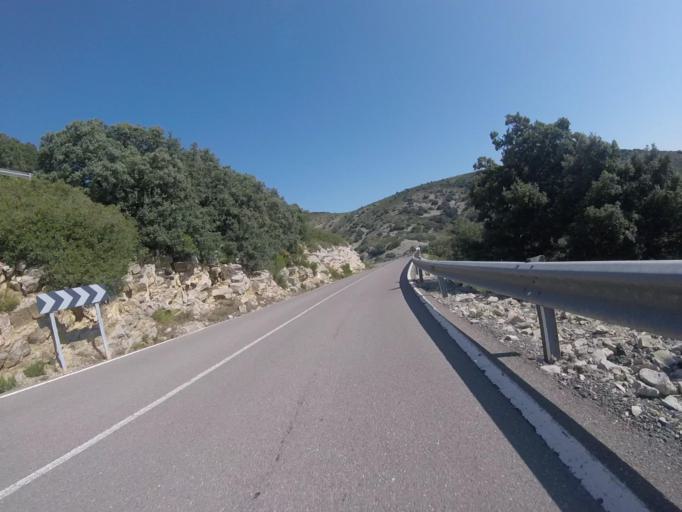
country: ES
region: Valencia
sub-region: Provincia de Castello
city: Benafigos
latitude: 40.2643
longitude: -0.2324
